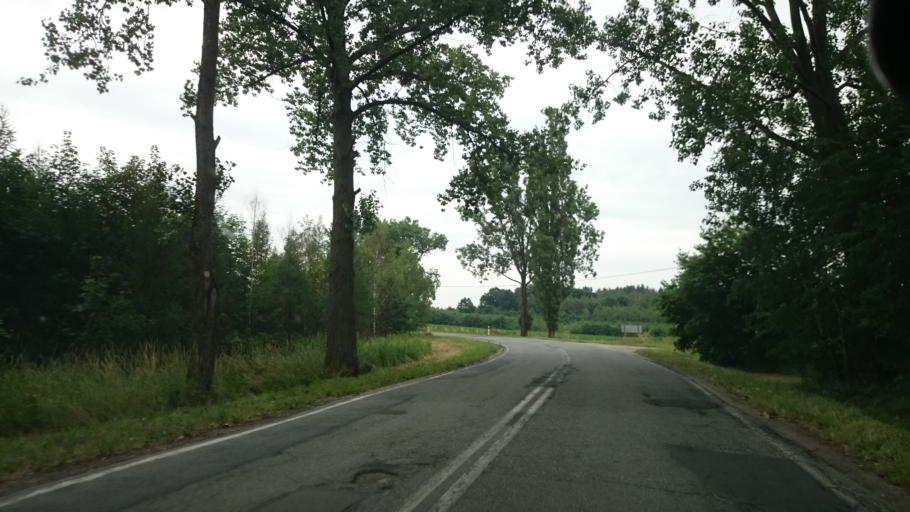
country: PL
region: Lower Silesian Voivodeship
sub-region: Powiat strzelinski
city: Przeworno
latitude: 50.6440
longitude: 17.1793
